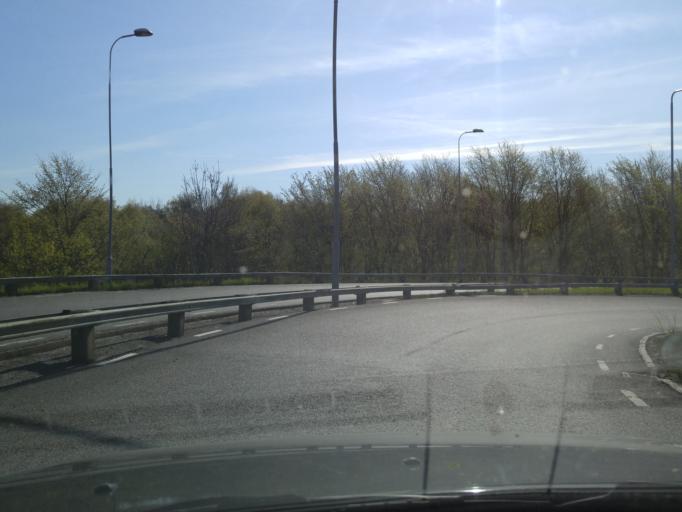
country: SE
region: Vaestra Goetaland
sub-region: Goteborg
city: Majorna
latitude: 57.6765
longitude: 11.9168
